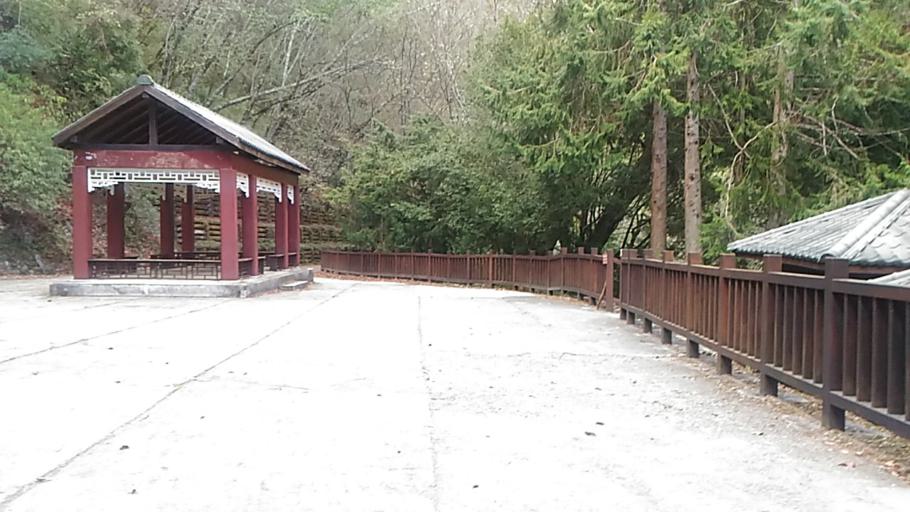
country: TW
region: Taiwan
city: Daxi
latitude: 24.4122
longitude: 121.3026
